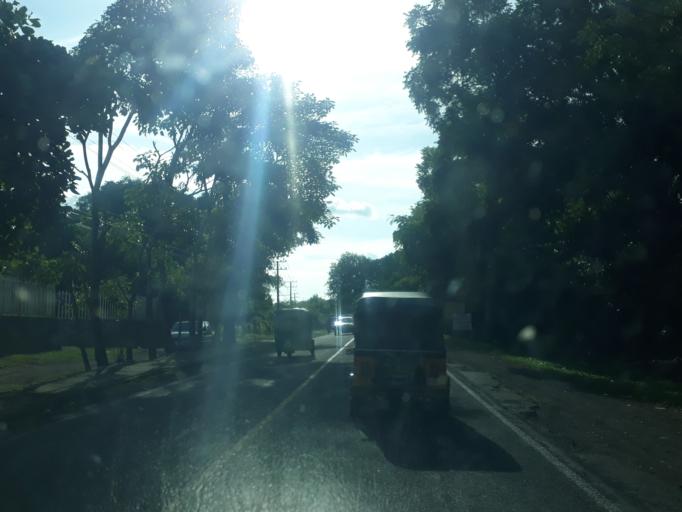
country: NI
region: Masaya
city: Masatepe
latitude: 11.9046
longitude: -86.1578
